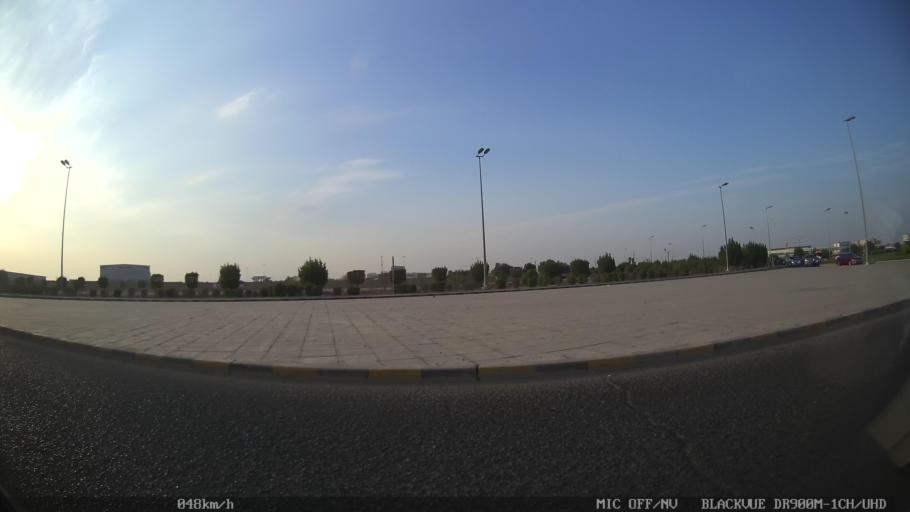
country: KW
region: Al Farwaniyah
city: Janub as Surrah
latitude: 29.2571
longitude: 48.0112
